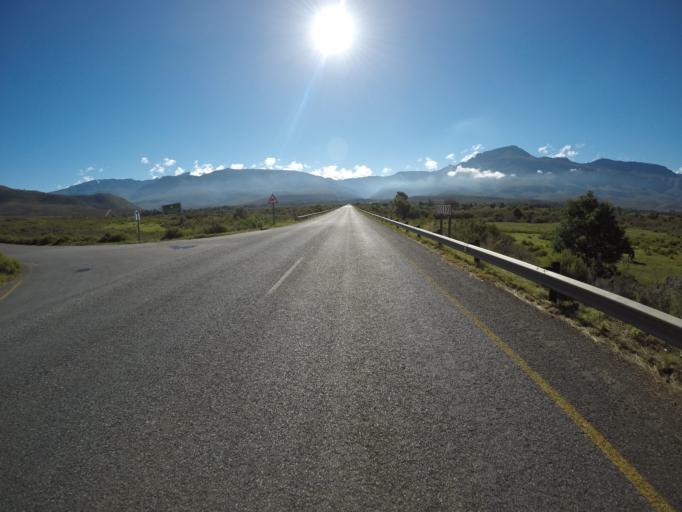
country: ZA
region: Western Cape
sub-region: Overberg District Municipality
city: Caledon
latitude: -34.0679
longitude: 19.5588
